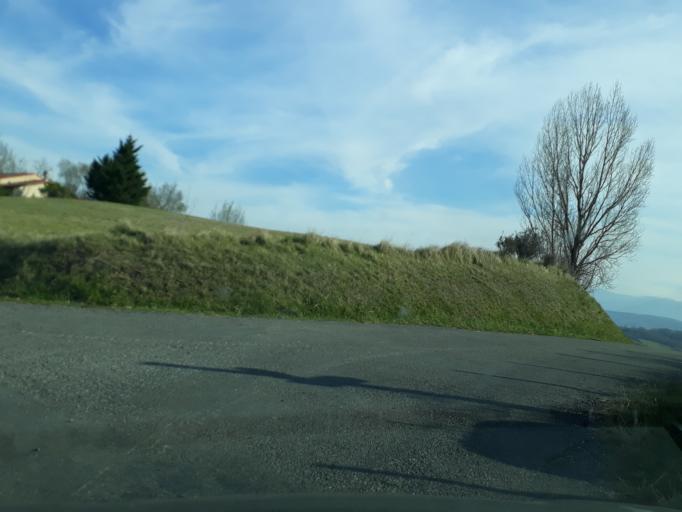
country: FR
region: Midi-Pyrenees
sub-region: Departement de la Haute-Garonne
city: Montesquieu-Volvestre
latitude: 43.1783
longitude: 1.3221
